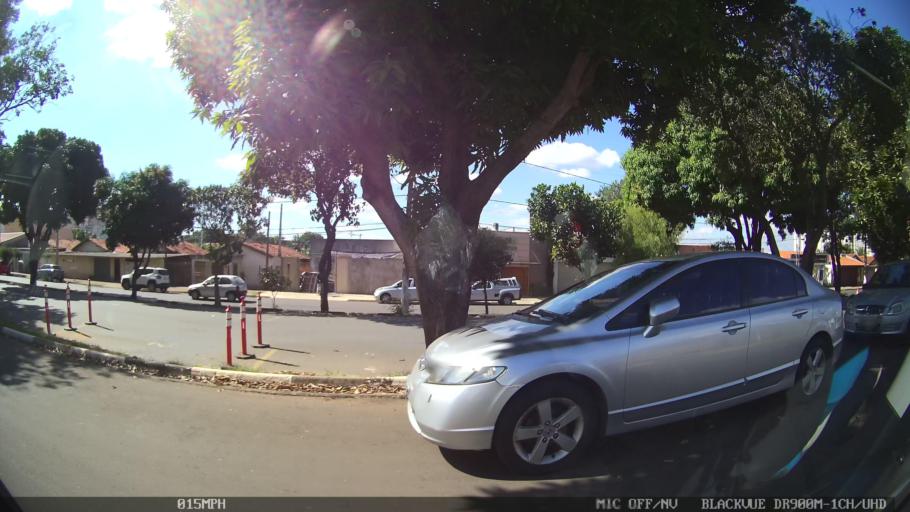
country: BR
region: Sao Paulo
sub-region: Hortolandia
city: Hortolandia
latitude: -22.8923
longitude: -47.2213
